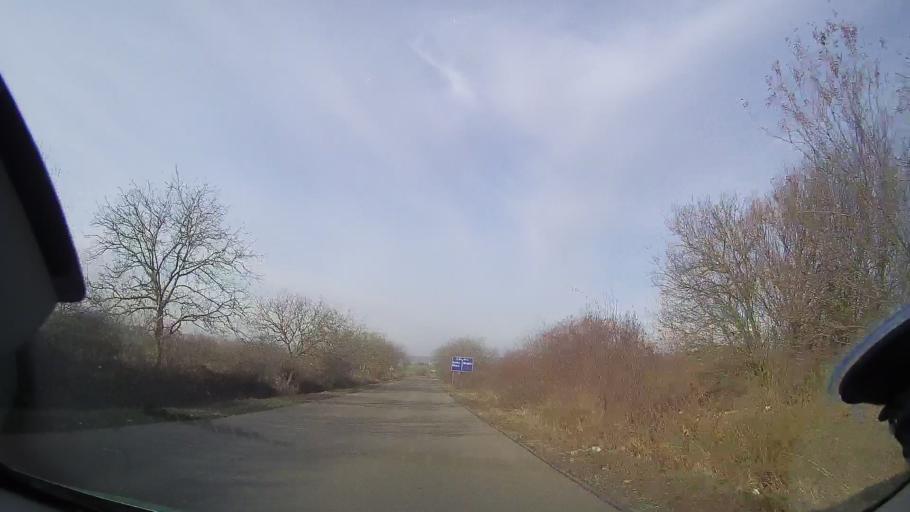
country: RO
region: Bihor
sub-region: Comuna Spinus
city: Spinus
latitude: 47.2256
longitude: 22.1680
